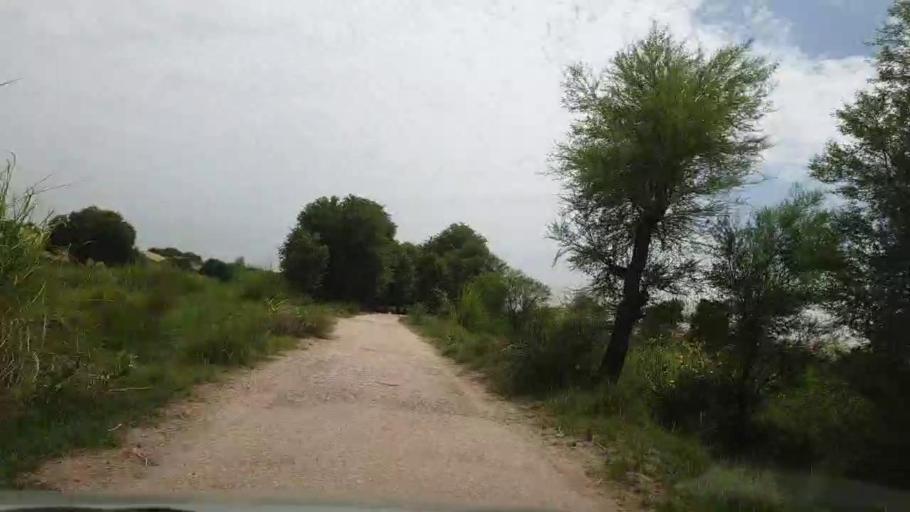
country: PK
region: Sindh
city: Bozdar
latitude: 27.0653
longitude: 68.9659
